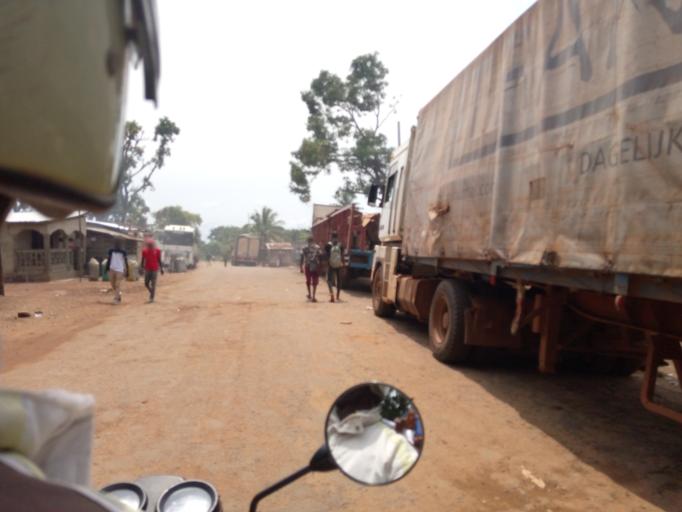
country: SL
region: Western Area
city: Waterloo
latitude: 8.3698
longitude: -13.0911
